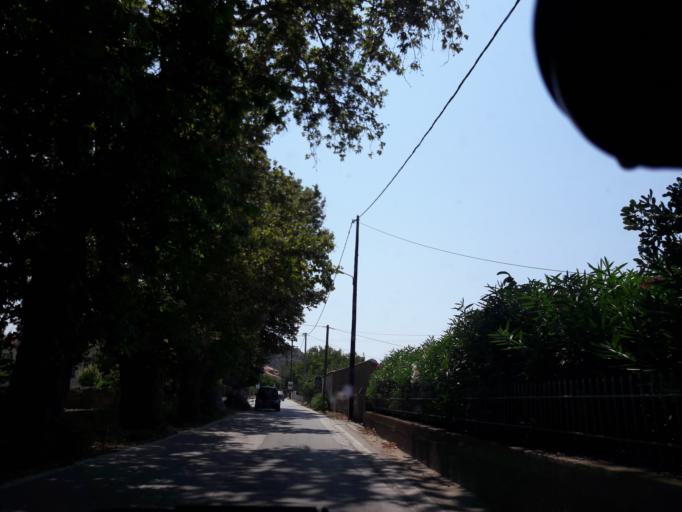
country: GR
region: North Aegean
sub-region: Nomos Lesvou
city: Myrina
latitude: 39.8675
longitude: 25.1529
